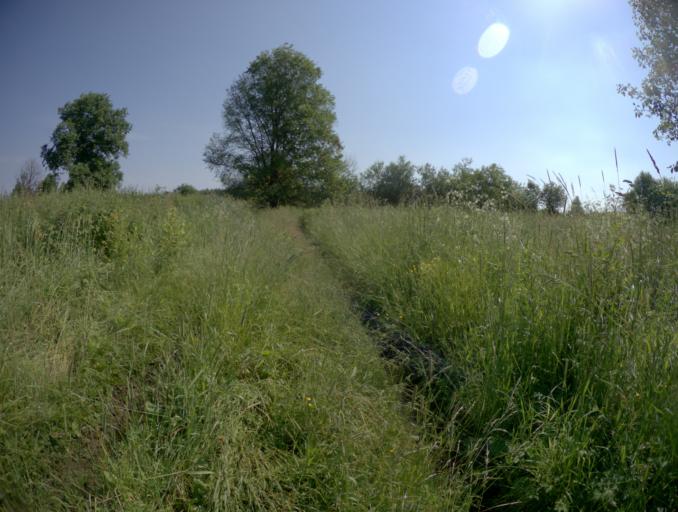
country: RU
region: Vladimir
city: Vyazniki
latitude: 56.3491
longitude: 42.1911
